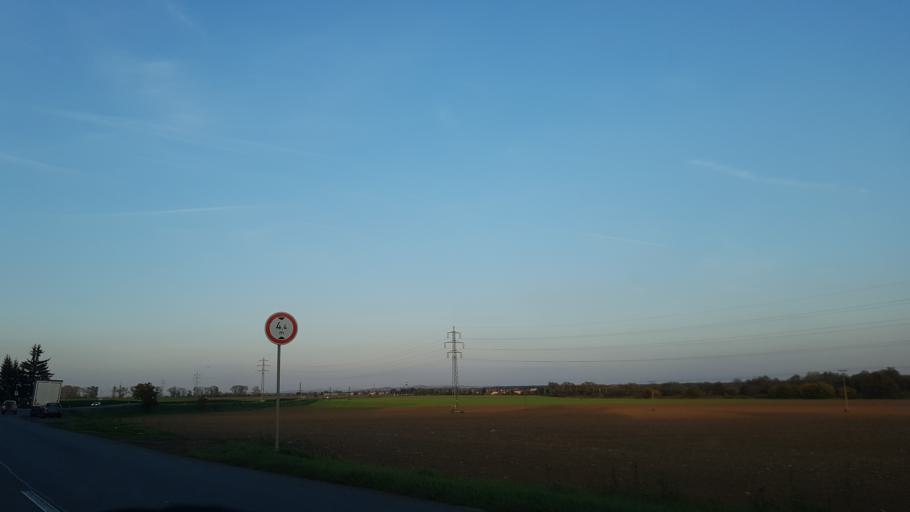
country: CZ
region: Zlin
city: Polesovice
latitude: 49.0245
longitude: 17.3546
